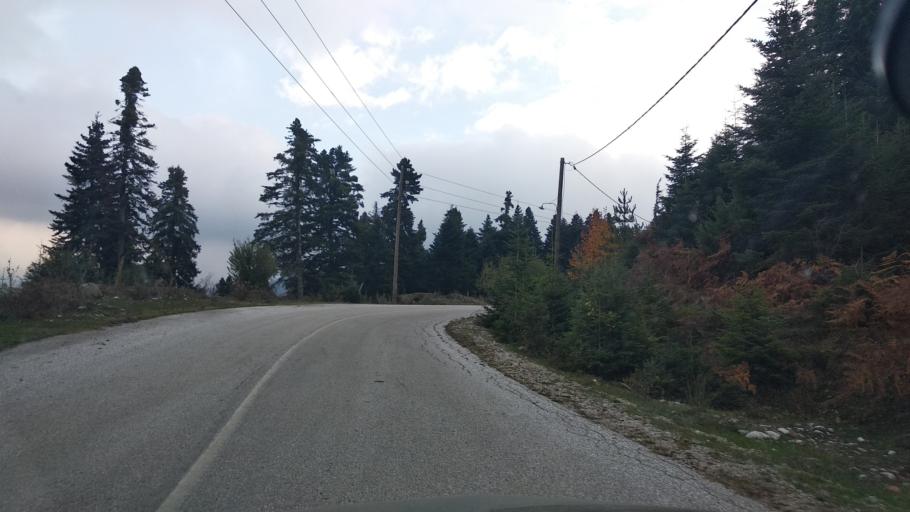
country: GR
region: Thessaly
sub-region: Trikala
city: Fiki
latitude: 39.5816
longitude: 21.4910
